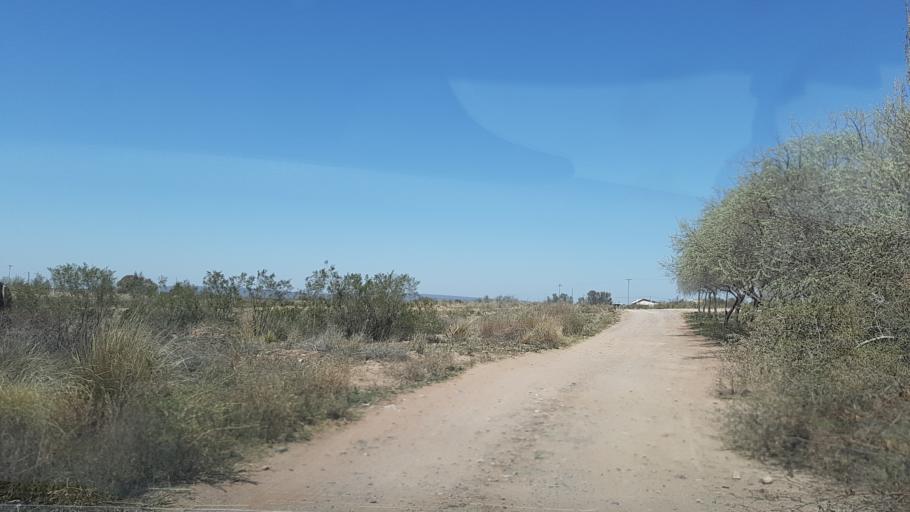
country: AR
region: Mendoza
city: Lujan de Cuyo
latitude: -33.0177
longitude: -68.9502
